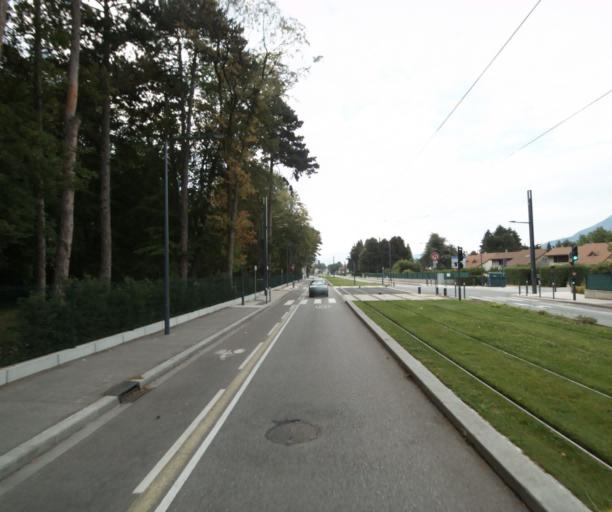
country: FR
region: Rhone-Alpes
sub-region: Departement de l'Isere
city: Fontanil-Cornillon
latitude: 45.2449
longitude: 5.6691
